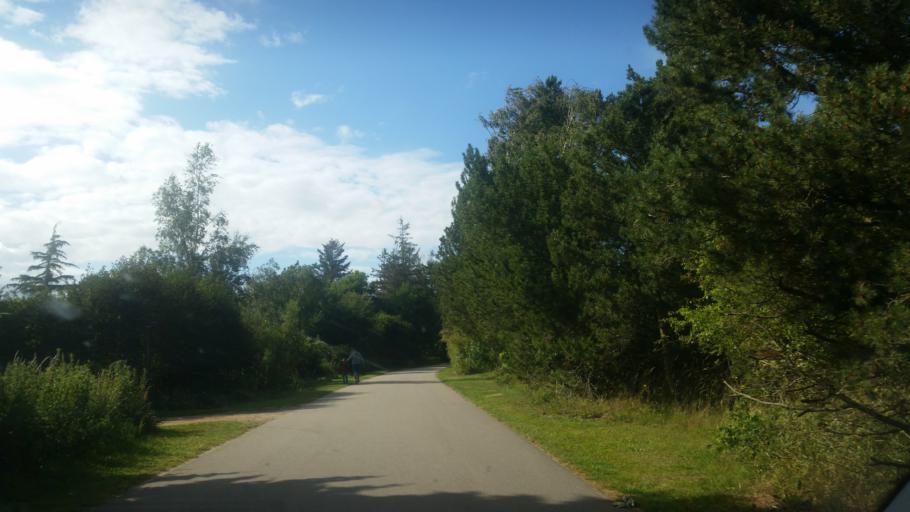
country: DK
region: Zealand
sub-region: Odsherred Kommune
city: Horve
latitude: 55.8274
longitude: 11.3973
